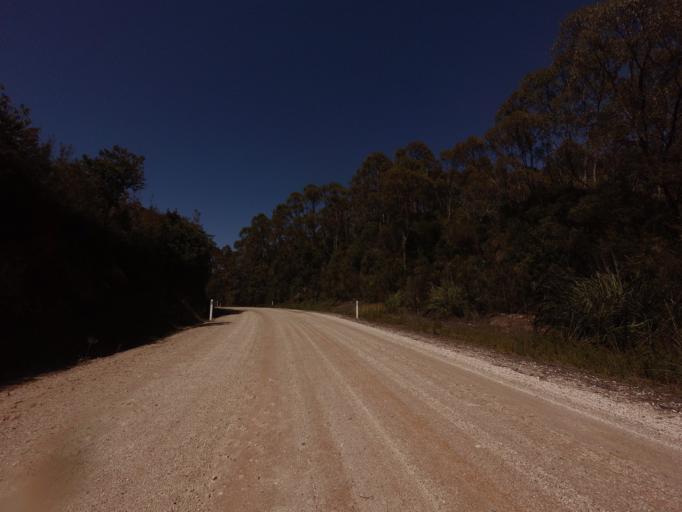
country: AU
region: Tasmania
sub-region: Huon Valley
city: Geeveston
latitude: -42.9842
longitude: 146.3638
